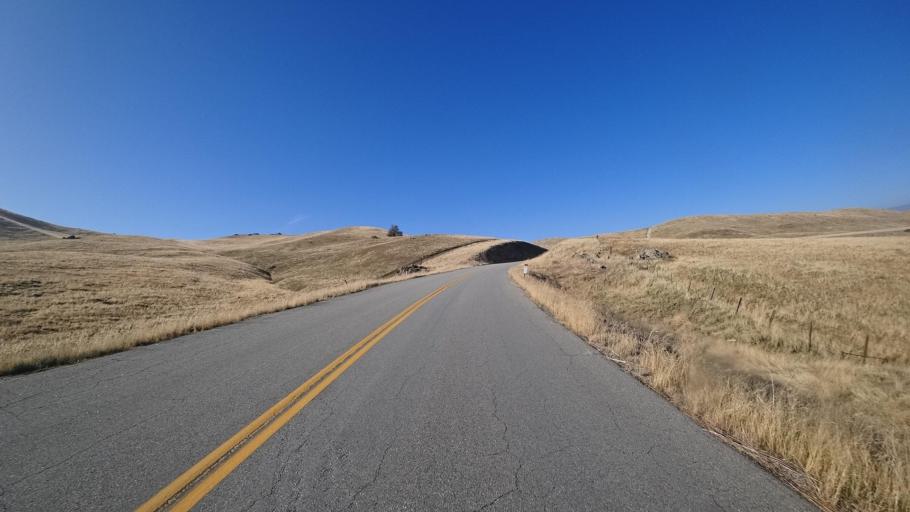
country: US
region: California
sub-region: Kern County
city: Bear Valley Springs
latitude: 35.2648
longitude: -118.6711
